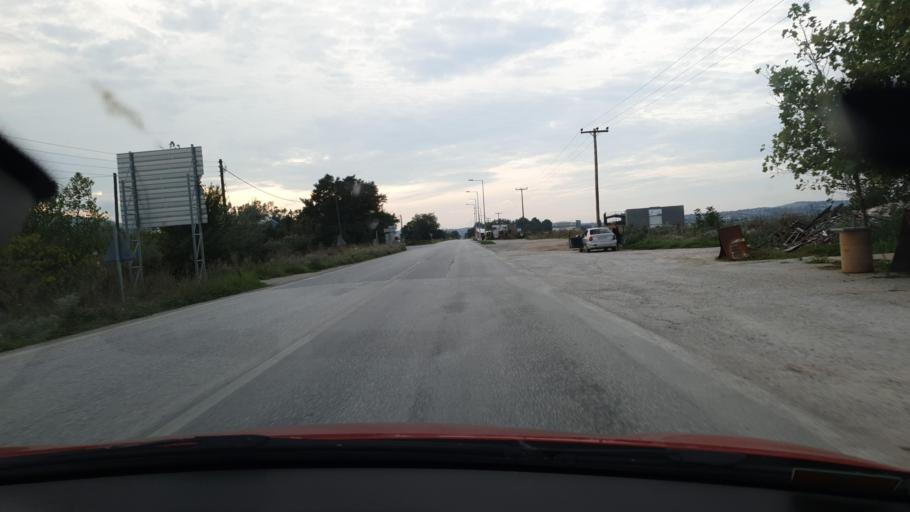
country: GR
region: Central Macedonia
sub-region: Nomos Thessalonikis
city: Liti
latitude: 40.7527
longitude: 22.9874
